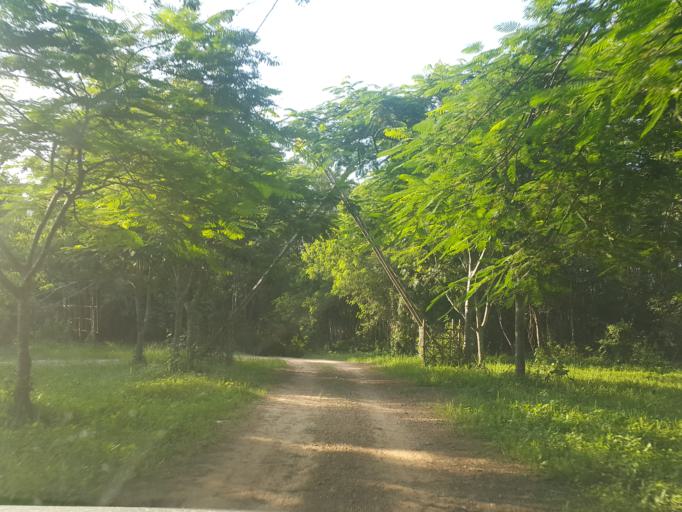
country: TH
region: Chiang Mai
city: Mae On
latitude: 18.6925
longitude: 99.2064
